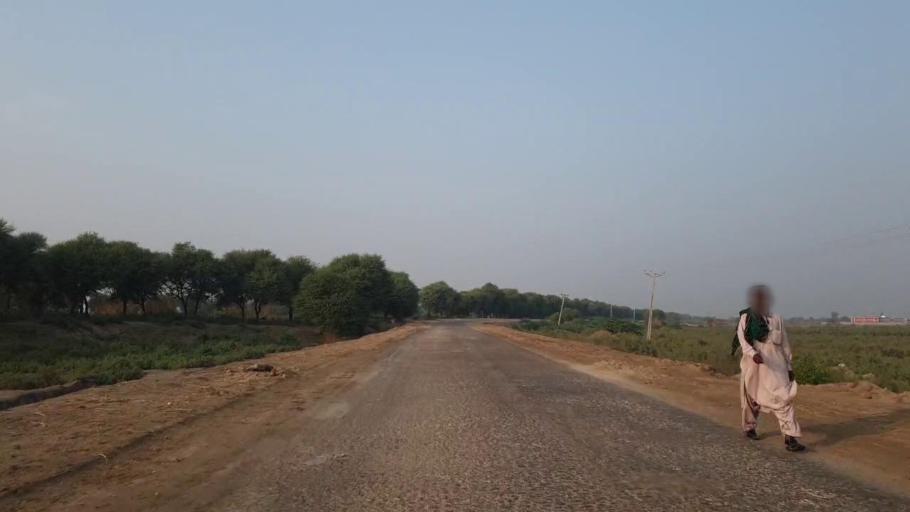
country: PK
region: Sindh
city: Tando Muhammad Khan
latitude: 25.1182
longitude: 68.4283
